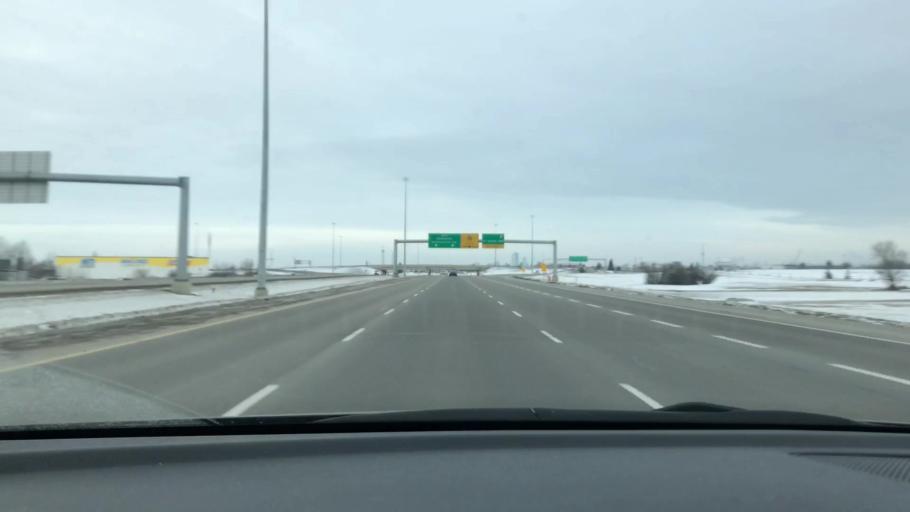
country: CA
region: Alberta
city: Sherwood Park
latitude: 53.5157
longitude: -113.3599
